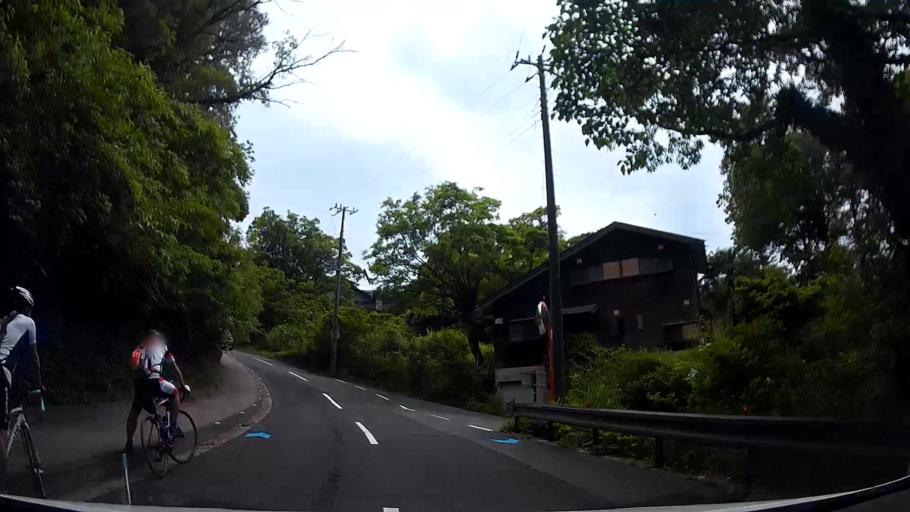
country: JP
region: Shizuoka
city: Ito
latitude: 34.8936
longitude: 139.1358
